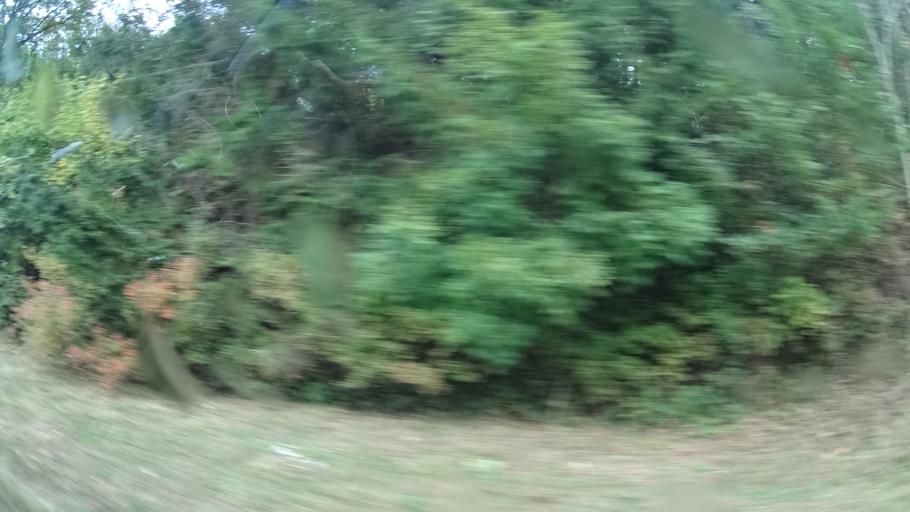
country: DE
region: Baden-Wuerttemberg
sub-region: Karlsruhe Region
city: Hardheim
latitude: 49.6125
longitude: 9.4625
